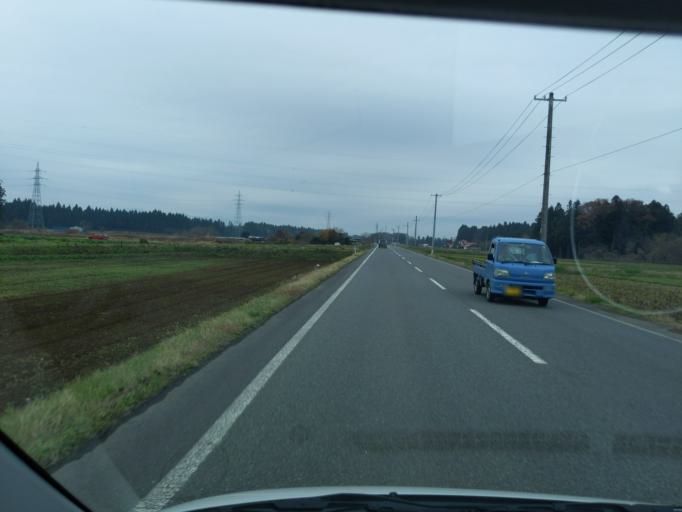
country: JP
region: Iwate
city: Mizusawa
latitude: 39.0947
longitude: 141.1260
